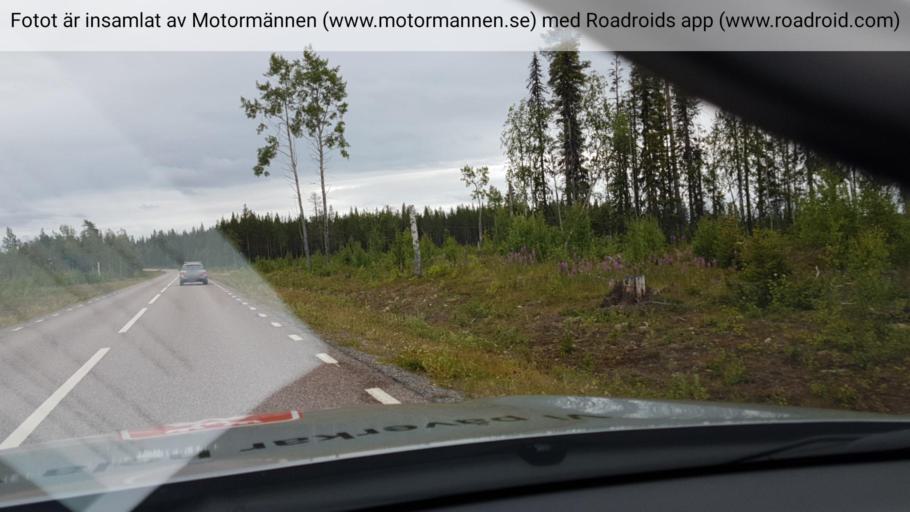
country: SE
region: Norrbotten
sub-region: Gallivare Kommun
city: Gaellivare
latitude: 67.0573
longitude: 21.5838
